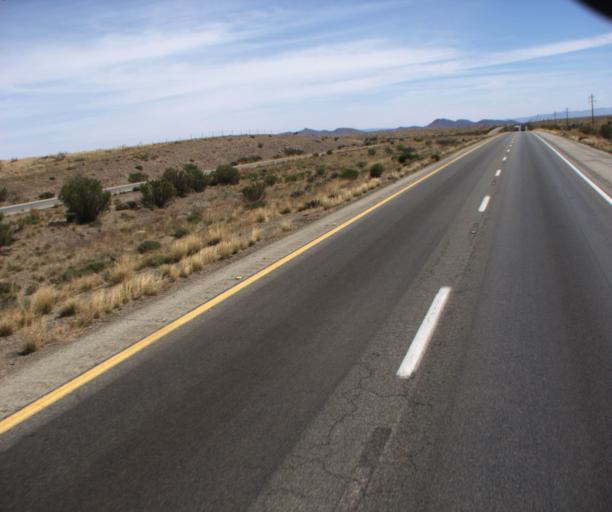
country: US
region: Arizona
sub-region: Cochise County
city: Willcox
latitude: 32.3522
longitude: -109.7220
